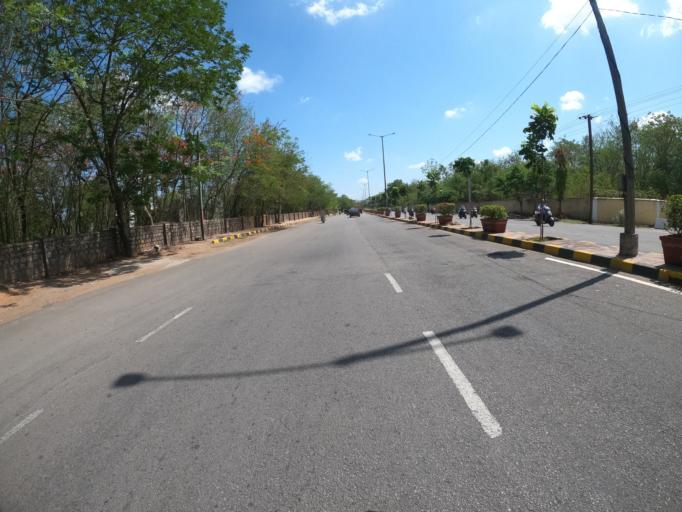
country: IN
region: Telangana
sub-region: Hyderabad
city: Hyderabad
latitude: 17.3852
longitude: 78.4225
